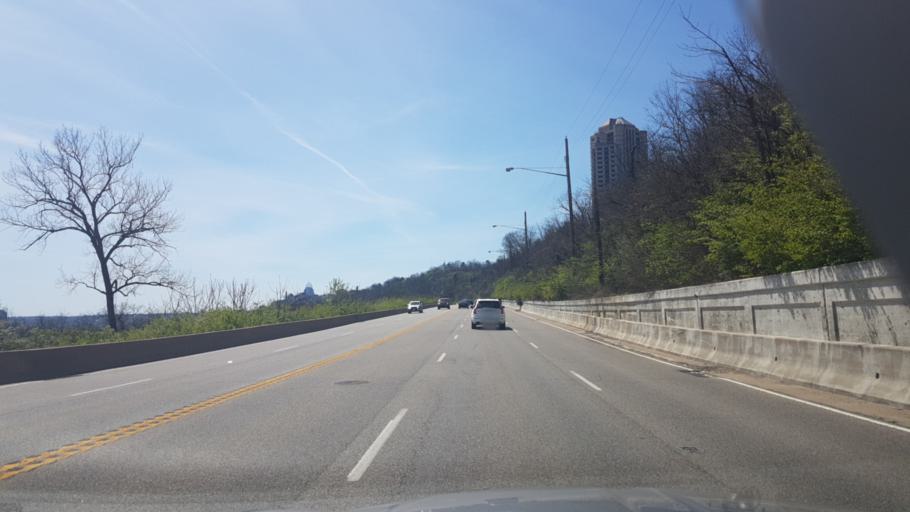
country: US
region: Kentucky
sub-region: Campbell County
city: Dayton
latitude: 39.1219
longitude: -84.4773
